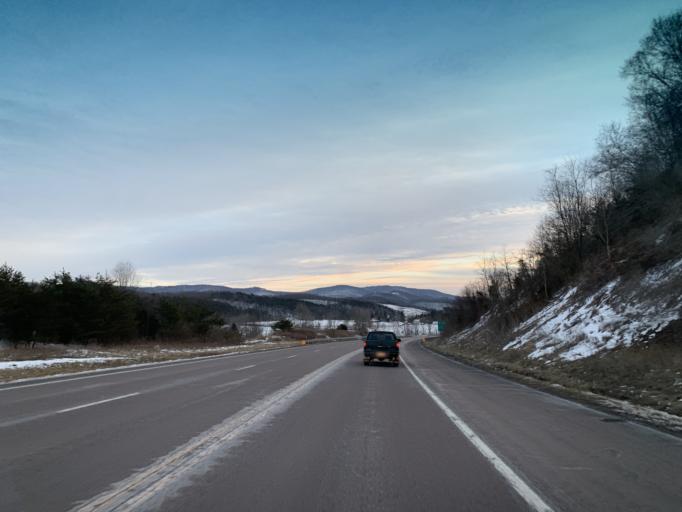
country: US
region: Maryland
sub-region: Allegany County
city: Cumberland
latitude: 39.6883
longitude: -78.7146
